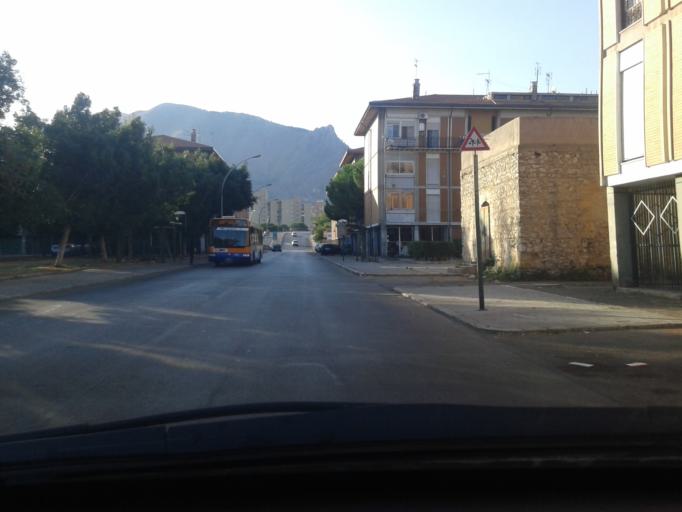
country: IT
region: Sicily
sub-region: Palermo
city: Palermo
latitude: 38.0900
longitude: 13.3595
